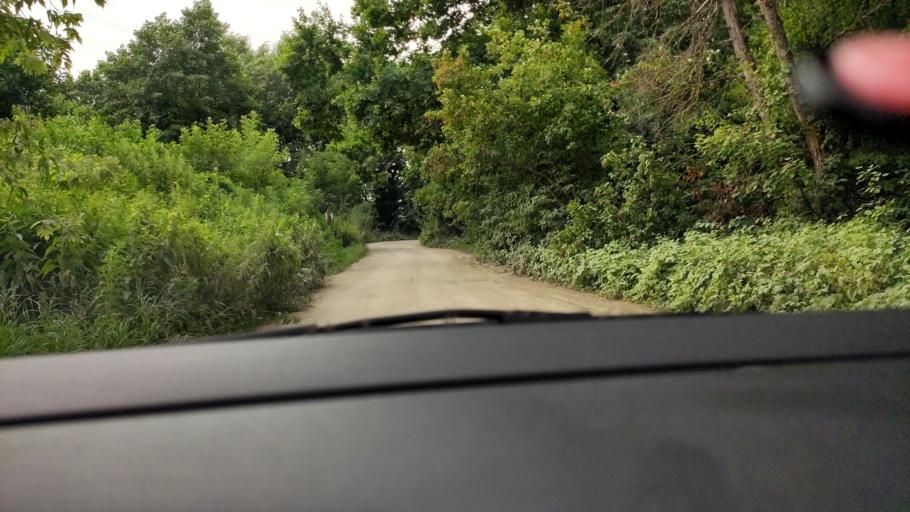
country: RU
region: Voronezj
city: Ramon'
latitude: 51.8912
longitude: 39.3525
